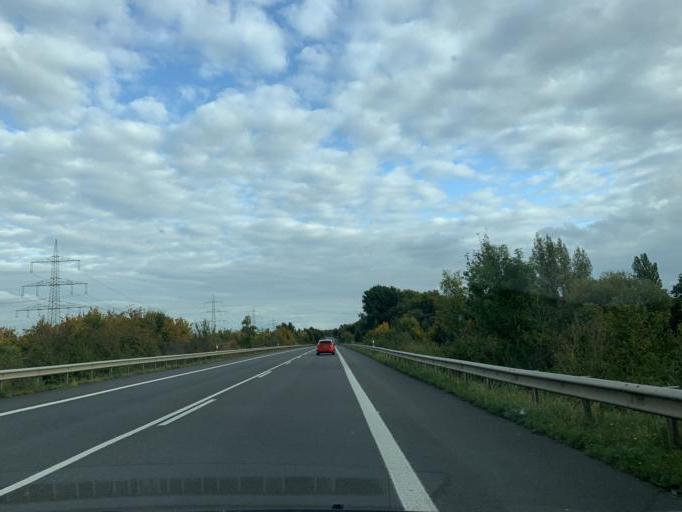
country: DE
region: North Rhine-Westphalia
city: Julich
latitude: 50.9008
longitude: 6.3698
